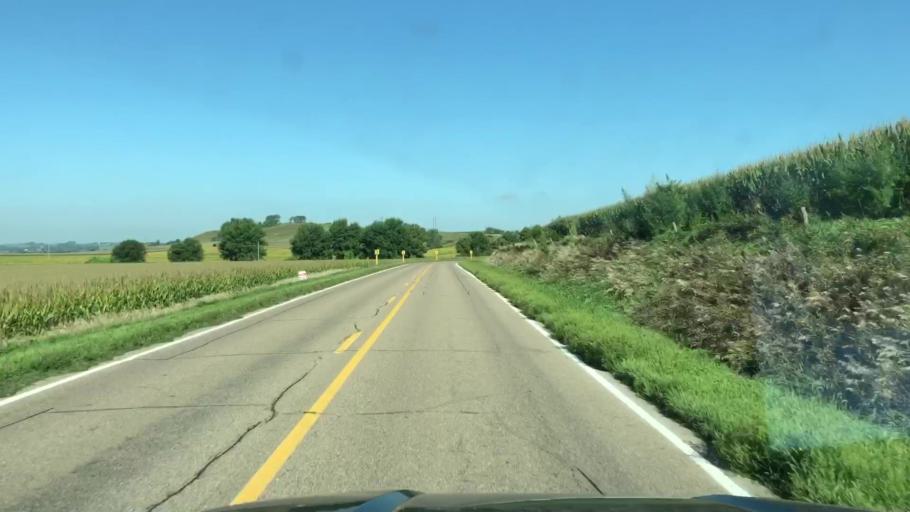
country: US
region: Iowa
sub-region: Woodbury County
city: Sergeant Bluff
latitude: 42.4080
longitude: -96.2543
